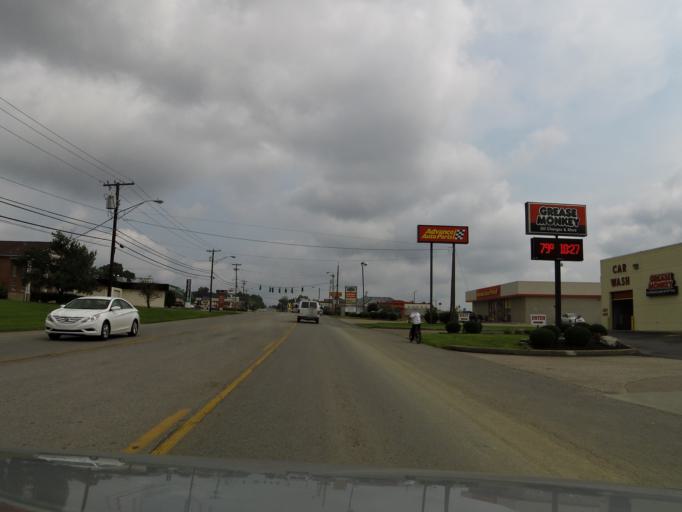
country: US
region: Kentucky
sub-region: Hopkins County
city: Madisonville
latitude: 37.3441
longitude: -87.4982
